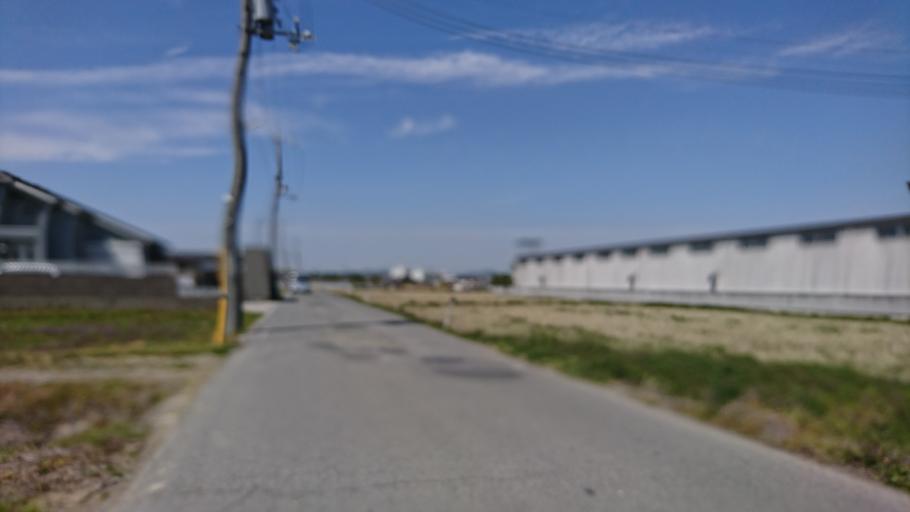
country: JP
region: Hyogo
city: Kakogawacho-honmachi
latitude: 34.7437
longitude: 134.8870
